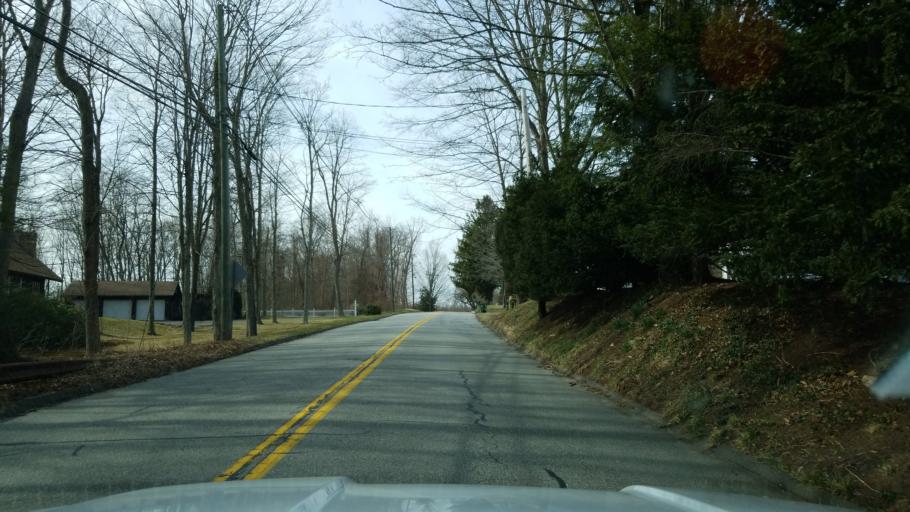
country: US
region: Connecticut
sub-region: Hartford County
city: Glastonbury Center
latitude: 41.6630
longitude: -72.5920
